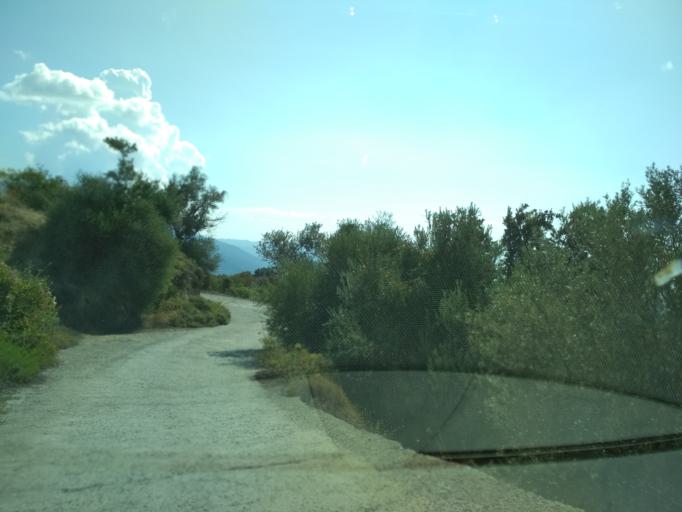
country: GR
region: Central Greece
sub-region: Nomos Evvoias
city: Oreoi
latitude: 38.8521
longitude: 23.1095
